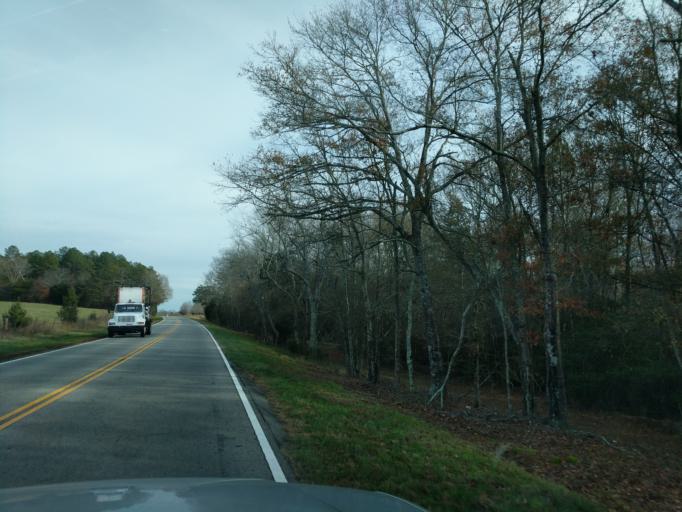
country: US
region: South Carolina
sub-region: Pickens County
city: Liberty
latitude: 34.7059
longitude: -82.6524
